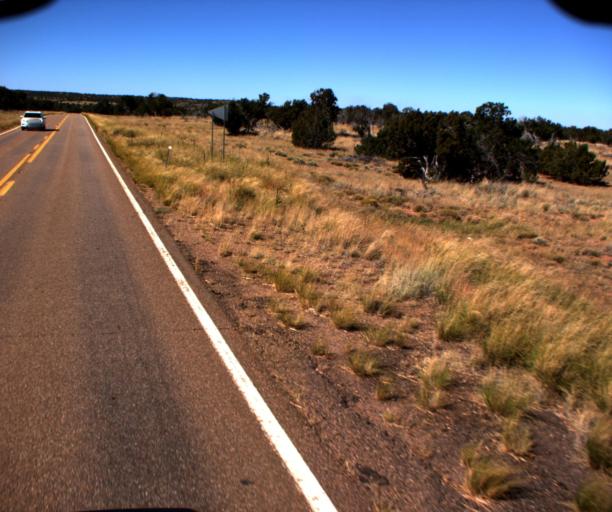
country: US
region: Arizona
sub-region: Navajo County
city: Heber-Overgaard
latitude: 34.4545
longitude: -110.4503
